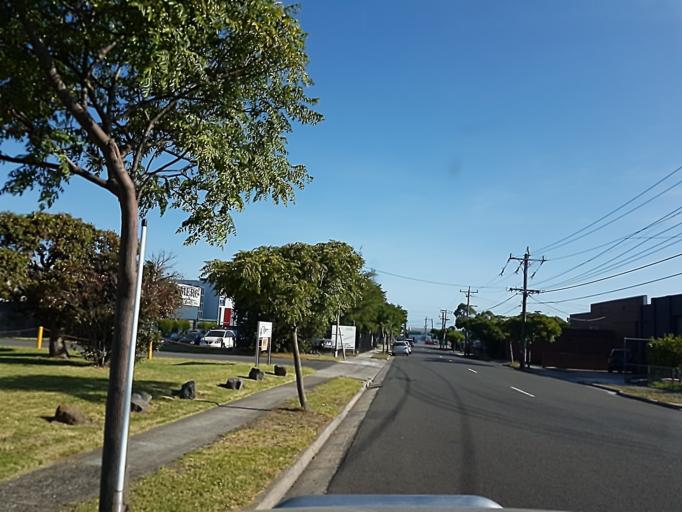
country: AU
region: Victoria
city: Clayton
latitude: -37.9107
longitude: 145.1099
